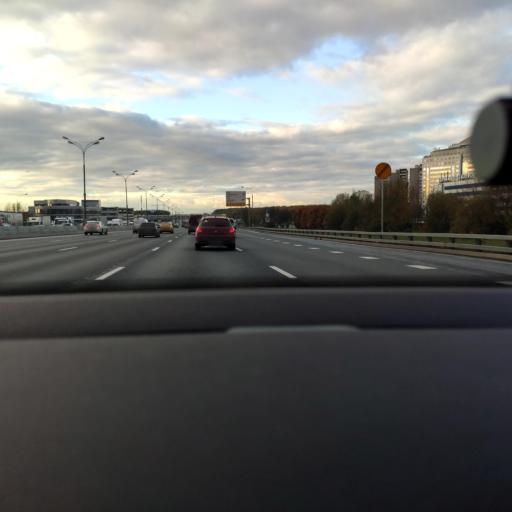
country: RU
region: Moskovskaya
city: Mosrentgen
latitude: 55.6272
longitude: 37.4724
